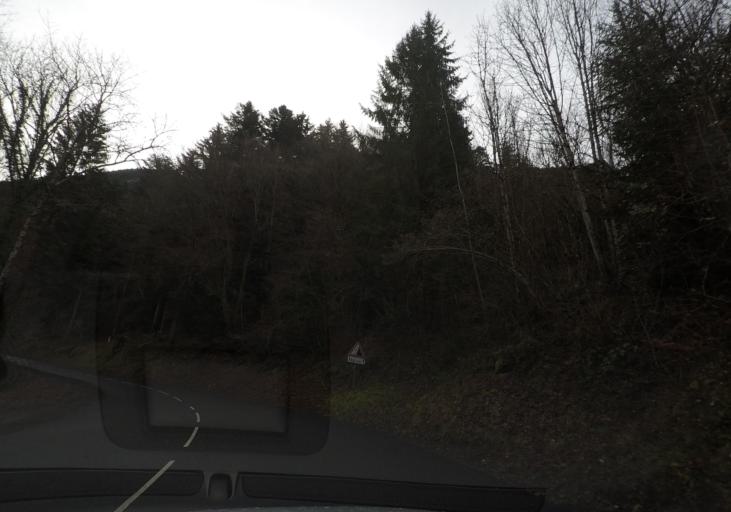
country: FR
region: Rhone-Alpes
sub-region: Departement de la Haute-Savoie
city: Ayse
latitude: 46.0601
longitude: 6.4363
